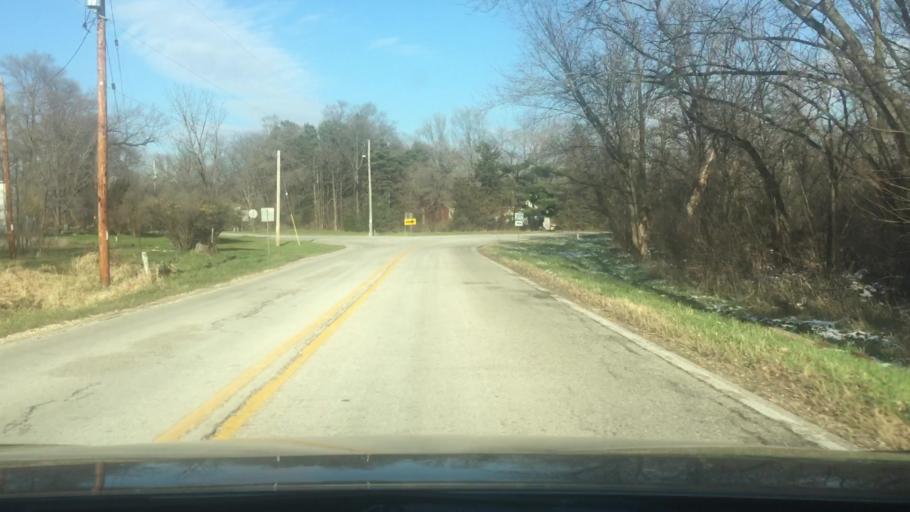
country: US
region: Wisconsin
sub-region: Waukesha County
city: Eagle
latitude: 42.9289
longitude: -88.4988
